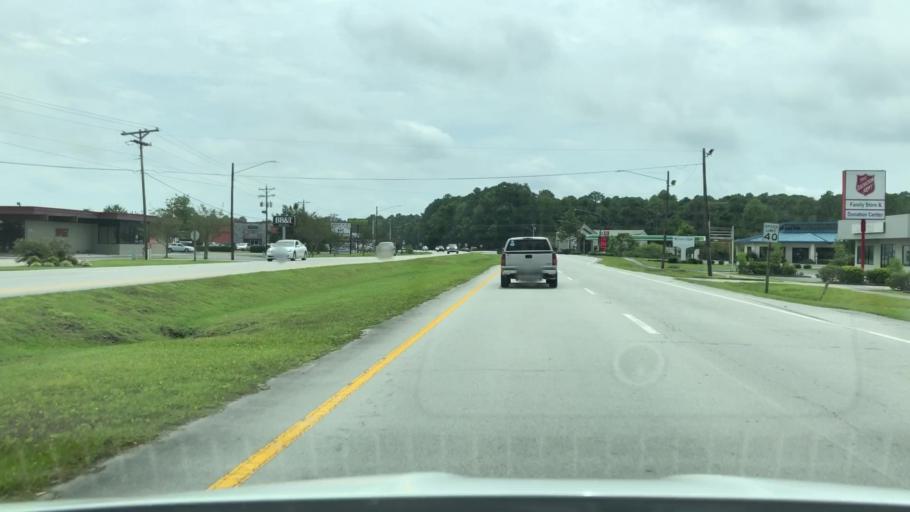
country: US
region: North Carolina
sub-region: Craven County
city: Havelock
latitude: 34.8596
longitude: -76.8971
